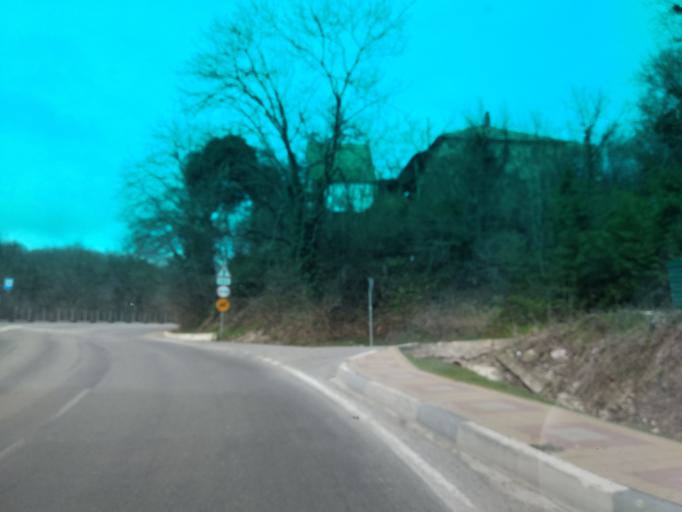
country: RU
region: Krasnodarskiy
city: Shepsi
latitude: 44.0419
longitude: 39.1425
